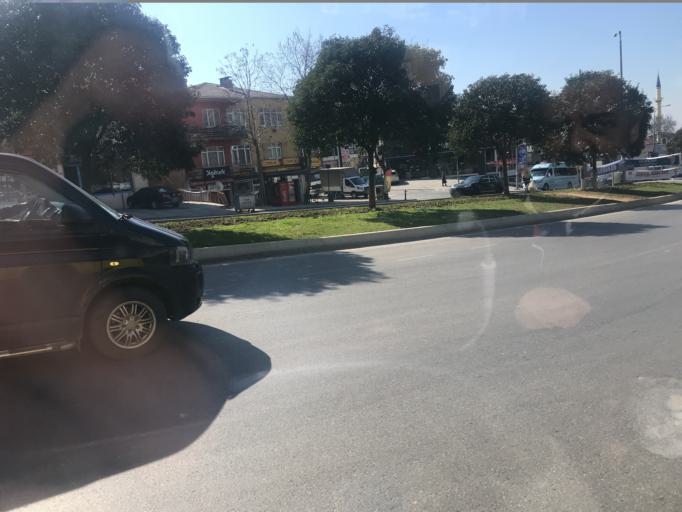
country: TR
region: Istanbul
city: Pendik
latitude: 40.8966
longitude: 29.2523
